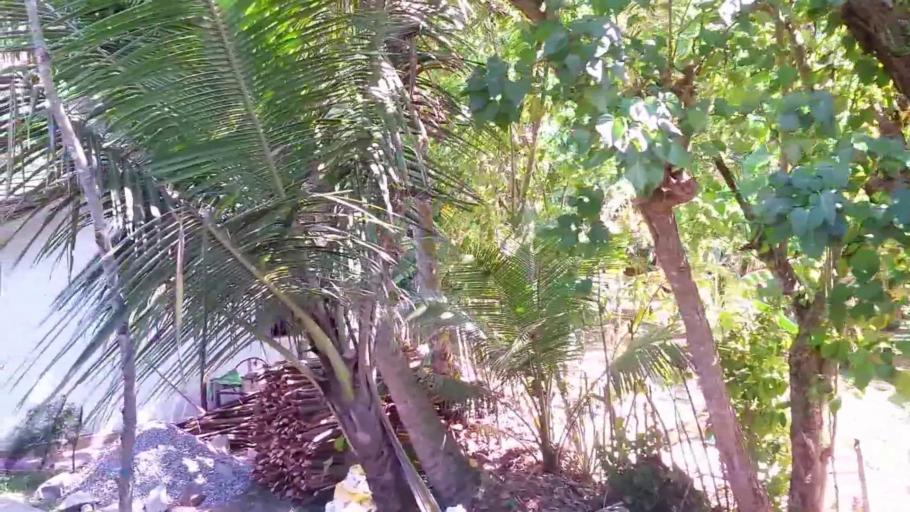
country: LK
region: Southern
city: Hikkaduwa
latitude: 6.1768
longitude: 80.0811
